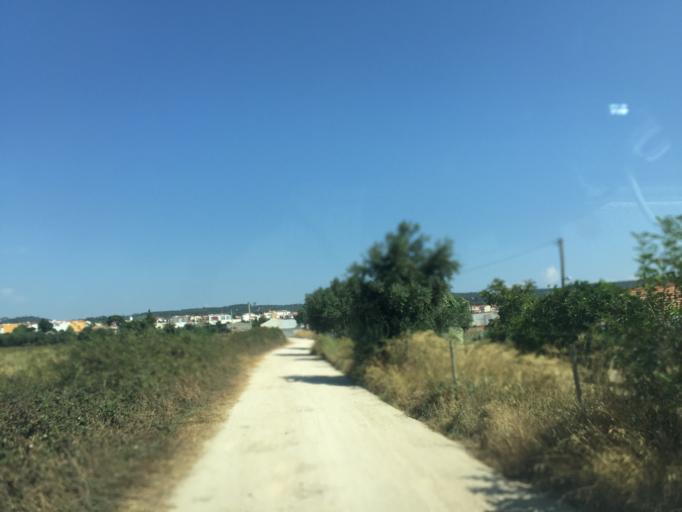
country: PT
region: Santarem
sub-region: Chamusca
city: Vila Nova da Barquinha
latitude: 39.4555
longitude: -8.4441
